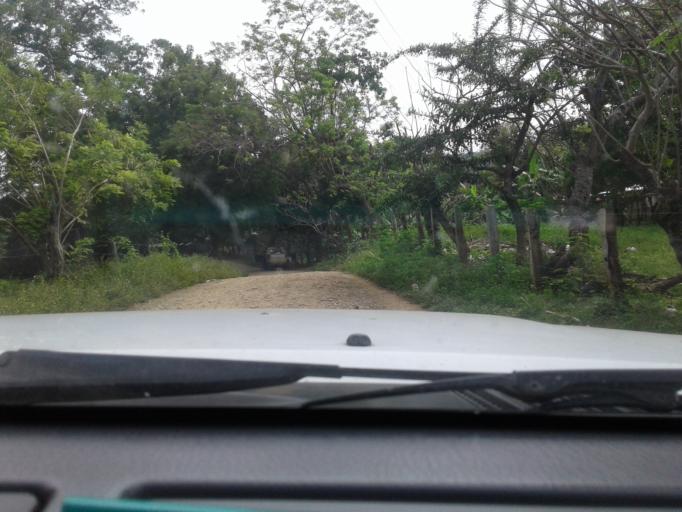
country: NI
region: Rivas
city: San Juan del Sur
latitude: 11.2034
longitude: -85.8035
